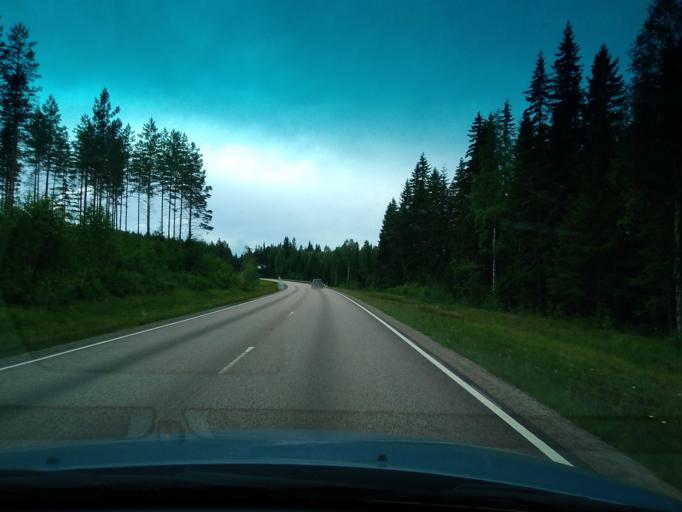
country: FI
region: Central Finland
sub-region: Keuruu
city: Multia
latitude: 62.3764
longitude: 24.7436
